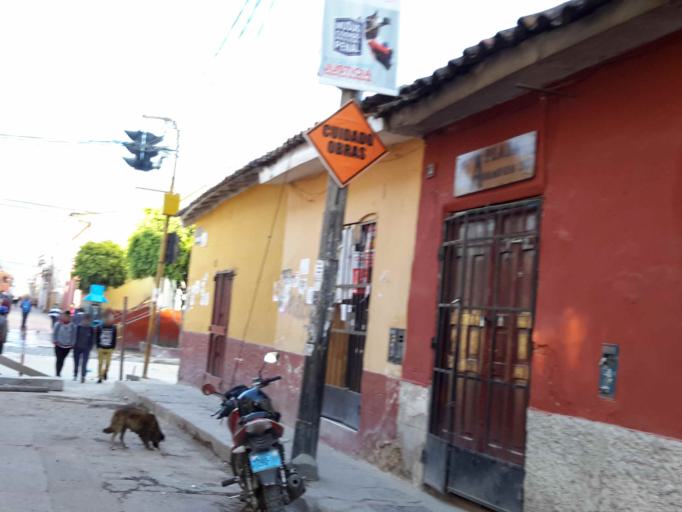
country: PE
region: Ayacucho
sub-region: Provincia de Huamanga
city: Ayacucho
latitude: -13.1573
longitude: -74.2245
